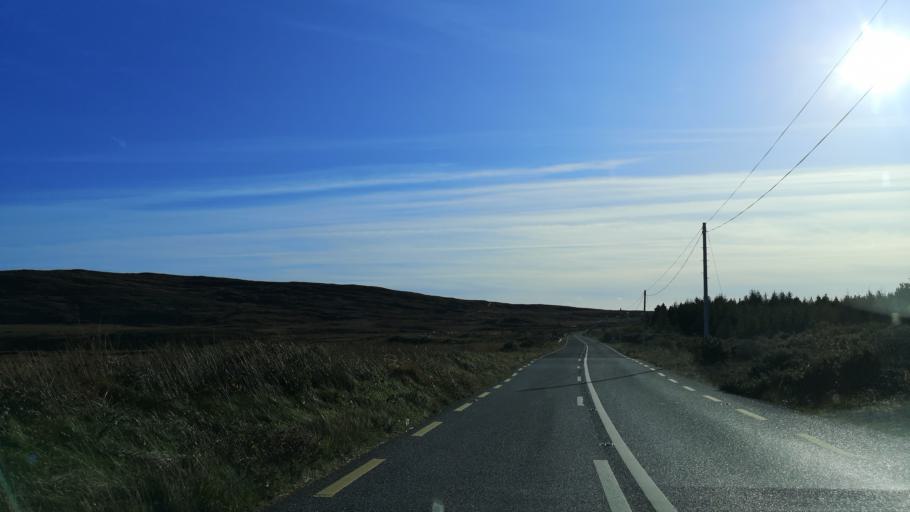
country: IE
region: Connaught
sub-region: County Galway
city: Clifden
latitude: 53.5357
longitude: -10.0374
